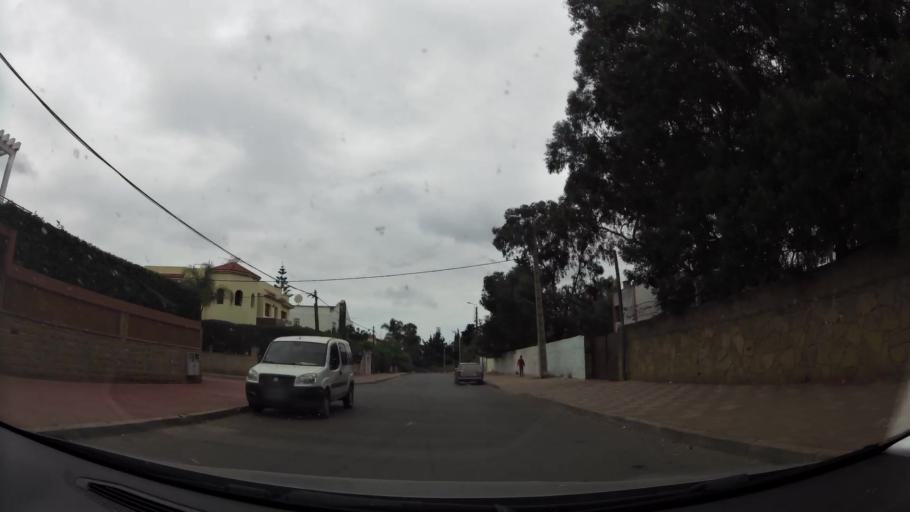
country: MA
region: Rabat-Sale-Zemmour-Zaer
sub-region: Rabat
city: Rabat
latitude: 33.9719
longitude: -6.8224
